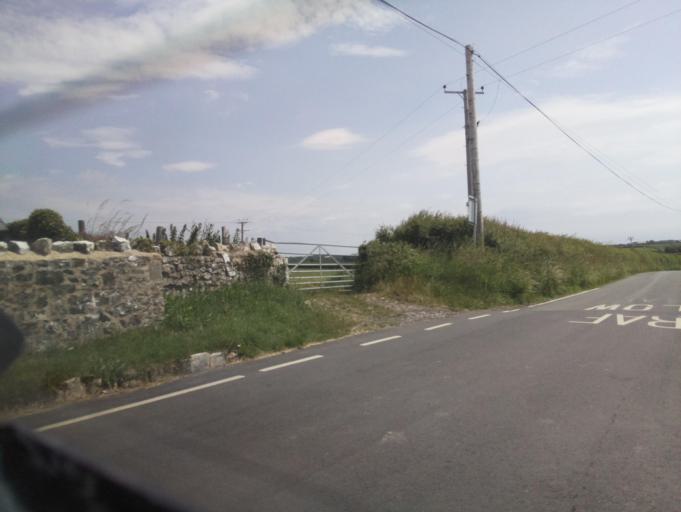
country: GB
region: Wales
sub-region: Vale of Glamorgan
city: Wick
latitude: 51.4186
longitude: -3.5495
